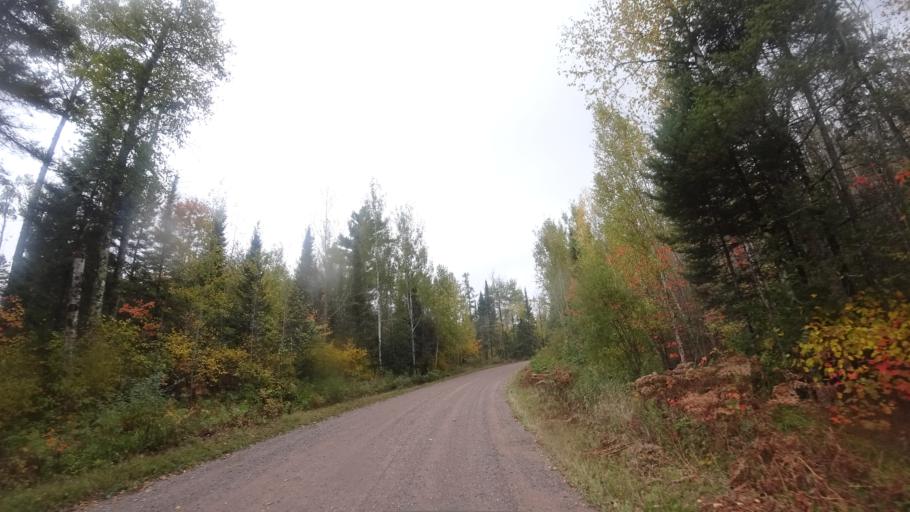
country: US
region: Wisconsin
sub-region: Sawyer County
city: Little Round Lake
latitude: 46.0513
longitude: -90.9959
